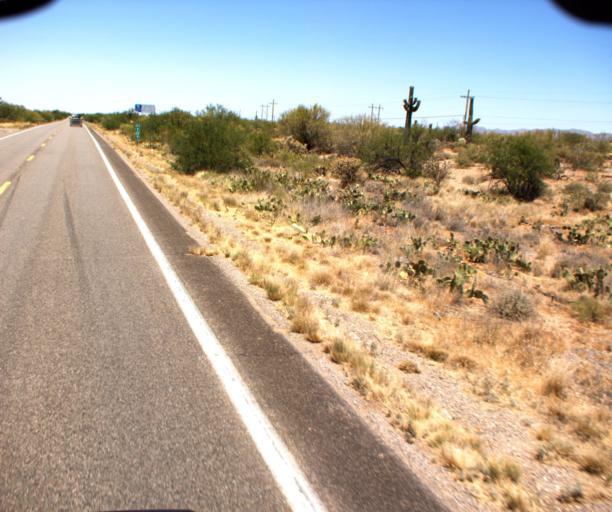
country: US
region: Arizona
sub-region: Pima County
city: Catalina
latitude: 32.7249
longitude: -111.1110
